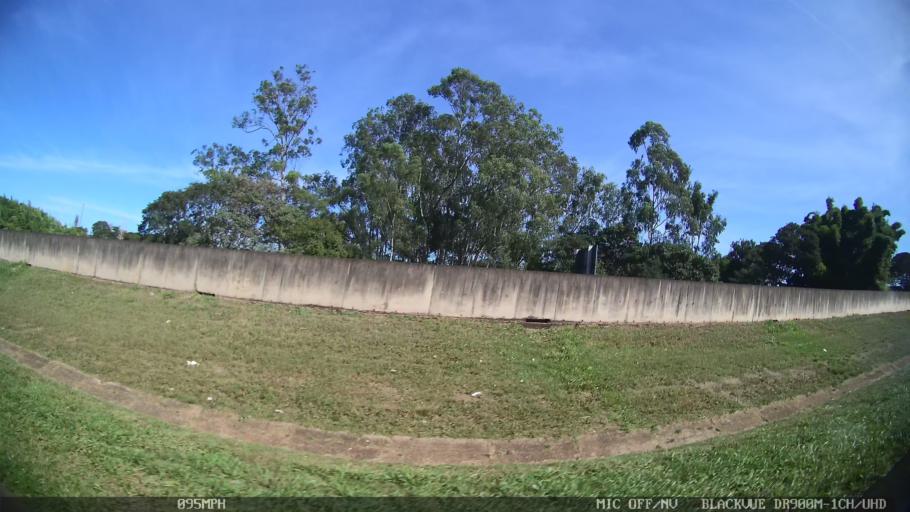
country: BR
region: Sao Paulo
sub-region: Pirassununga
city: Pirassununga
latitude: -21.9926
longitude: -47.4476
